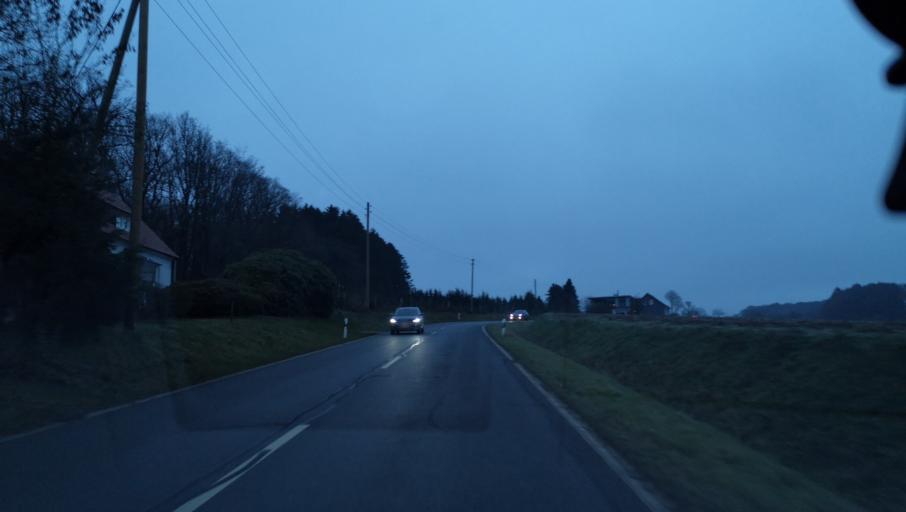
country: DE
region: North Rhine-Westphalia
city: Radevormwald
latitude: 51.2117
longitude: 7.3737
